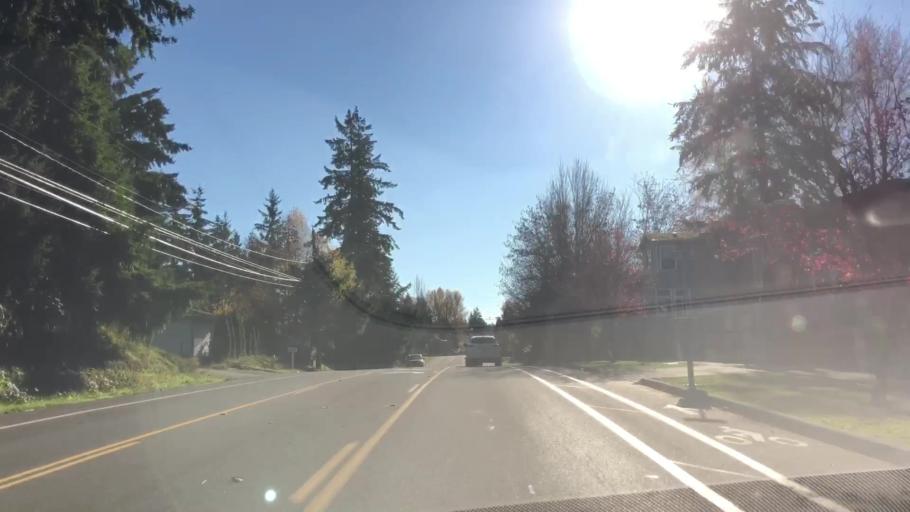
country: US
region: Washington
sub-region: King County
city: Kirkland
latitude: 47.6917
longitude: -122.1758
